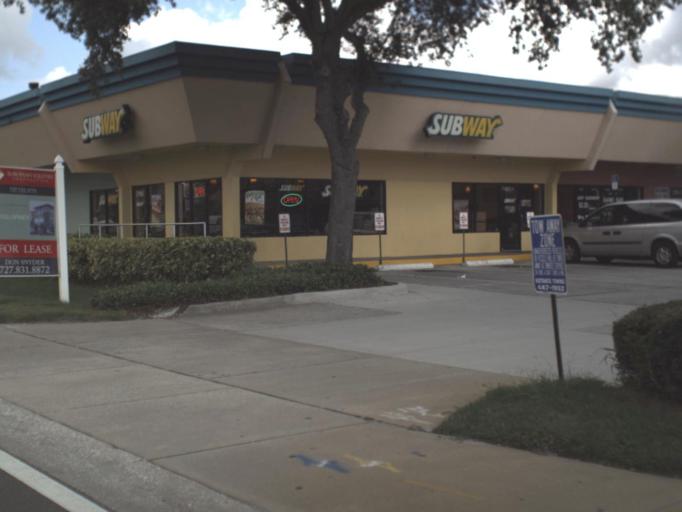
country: US
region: Florida
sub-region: Pinellas County
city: Safety Harbor
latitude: 27.9607
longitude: -82.7220
